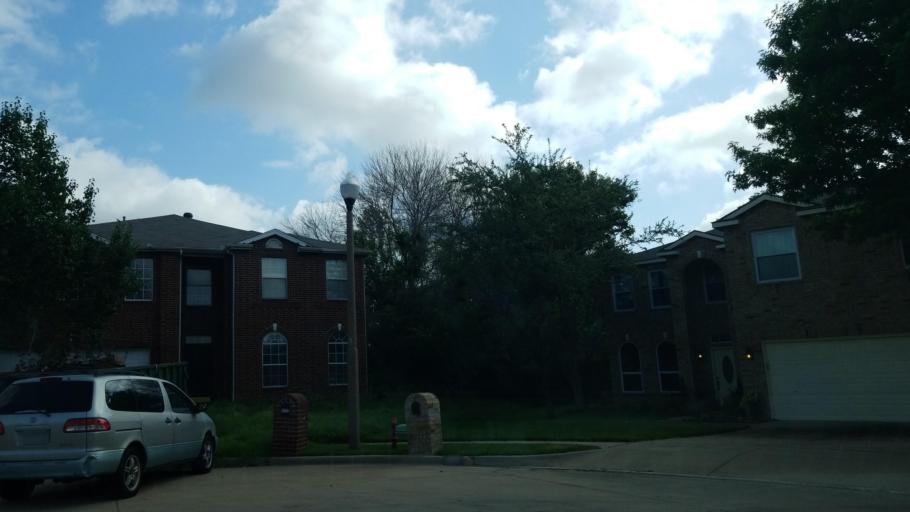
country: US
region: Texas
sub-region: Denton County
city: Corinth
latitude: 33.1463
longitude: -97.1138
